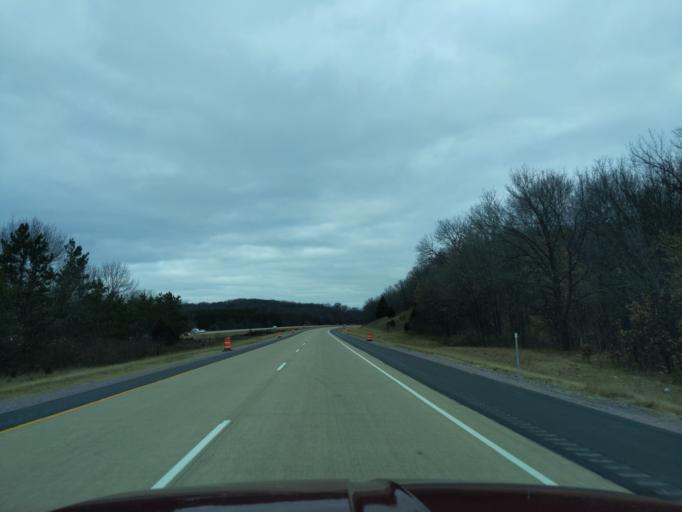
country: US
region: Wisconsin
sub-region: Columbia County
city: Portage
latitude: 43.6081
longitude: -89.4709
